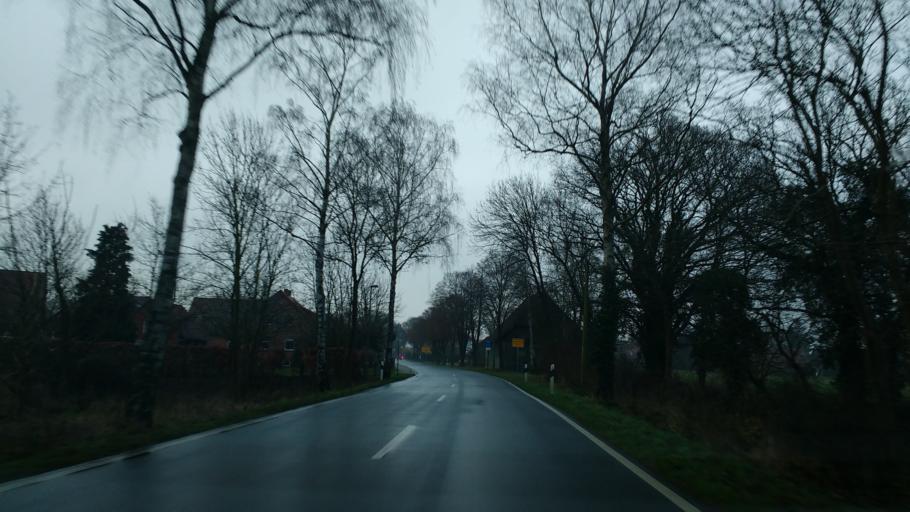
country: DE
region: Lower Saxony
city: Gilten
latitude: 52.6426
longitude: 9.5688
